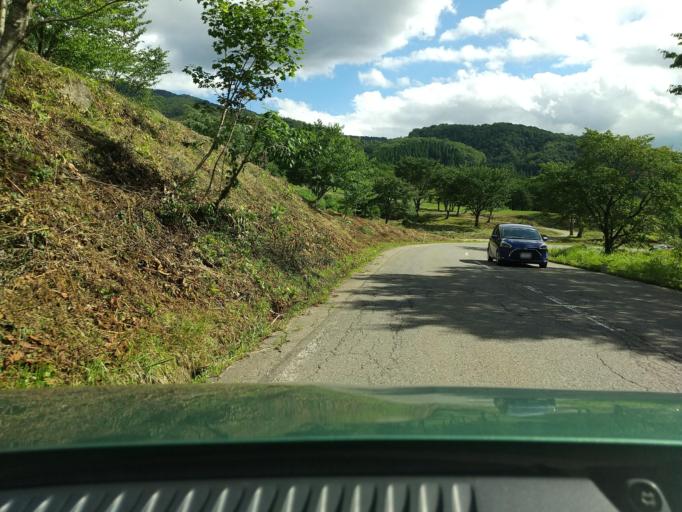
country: JP
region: Iwate
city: Shizukuishi
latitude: 39.7637
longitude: 140.7467
